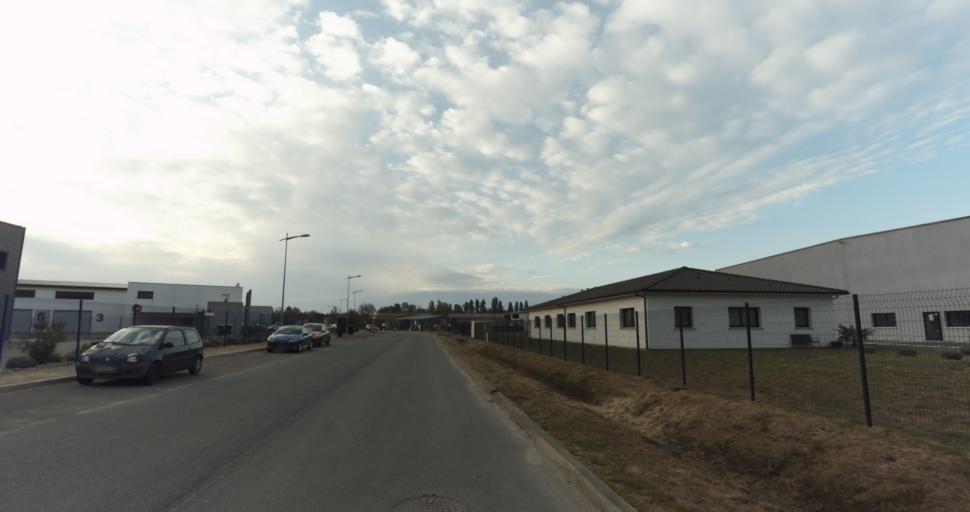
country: FR
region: Aquitaine
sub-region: Departement de la Gironde
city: Martignas-sur-Jalle
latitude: 44.7850
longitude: -0.7776
